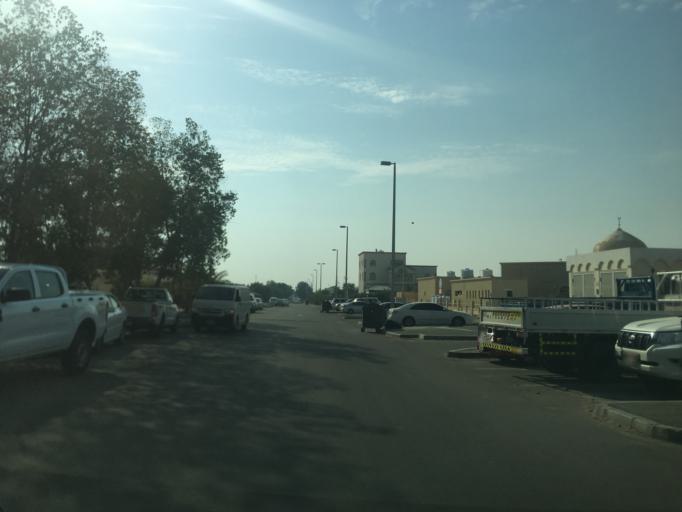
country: AE
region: Abu Dhabi
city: Abu Dhabi
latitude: 24.2996
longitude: 54.6513
